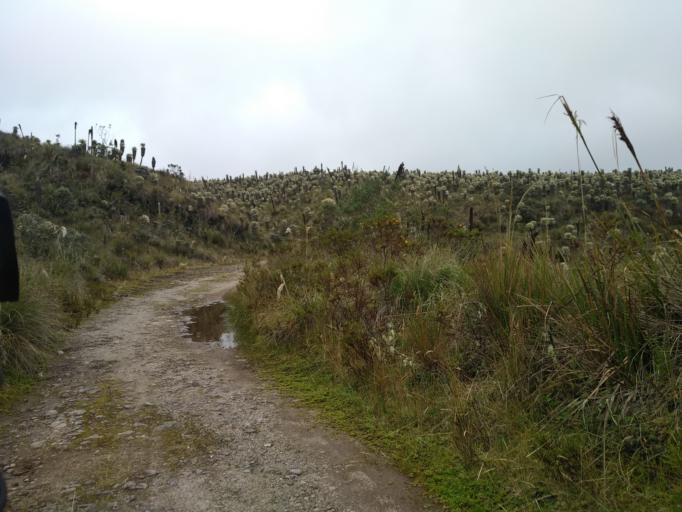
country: EC
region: Carchi
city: San Gabriel
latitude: 0.6859
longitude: -77.8505
